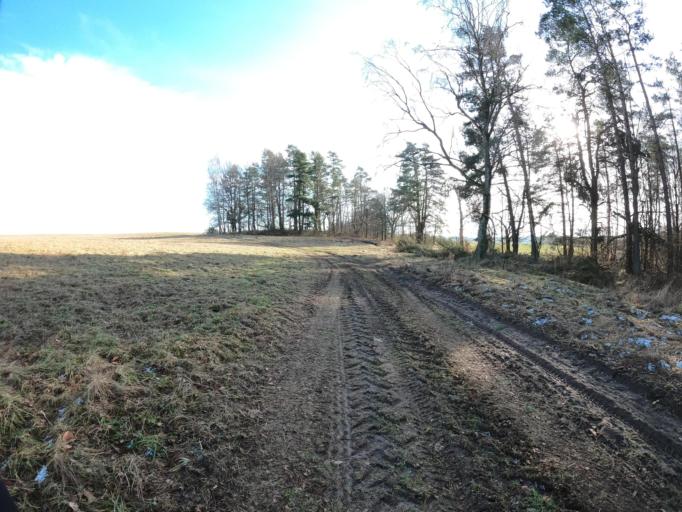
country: PL
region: West Pomeranian Voivodeship
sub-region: Powiat koszalinski
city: Polanow
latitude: 54.2079
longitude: 16.6494
